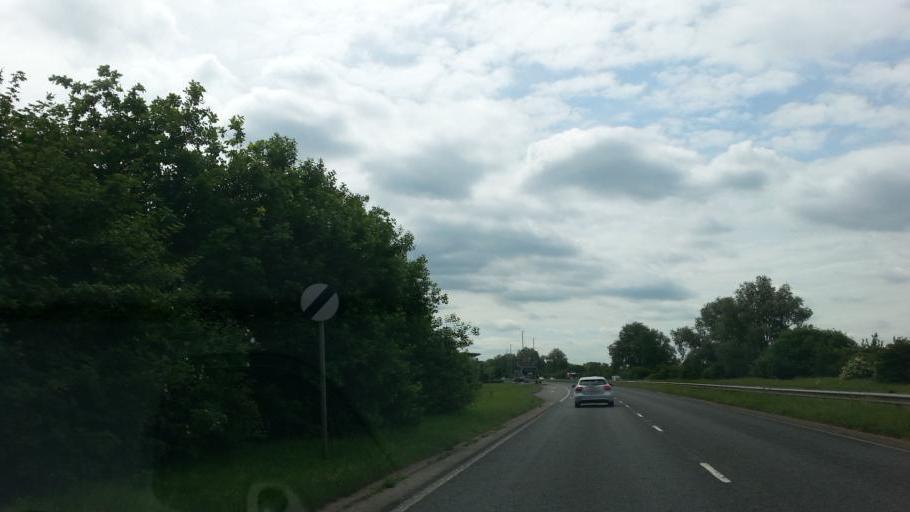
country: GB
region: England
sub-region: Leicestershire
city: Syston
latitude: 52.6940
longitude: -1.0963
